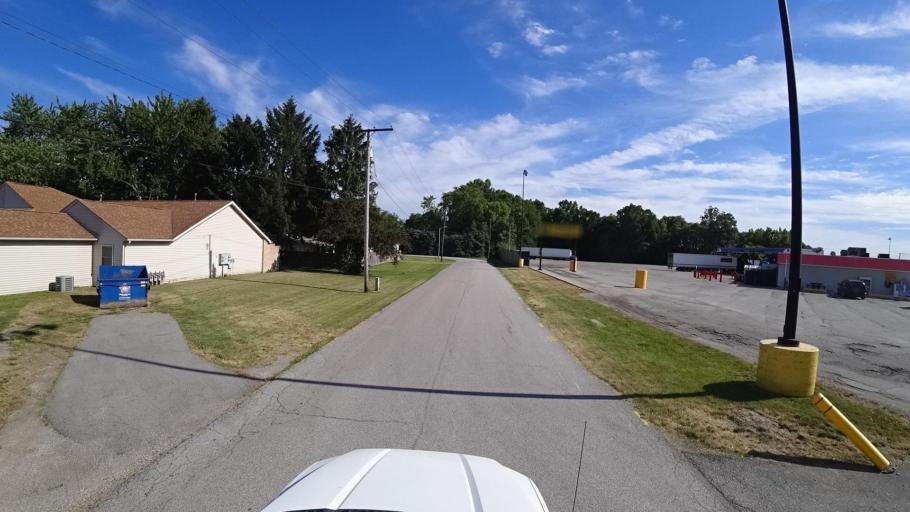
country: US
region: Indiana
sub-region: Porter County
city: Porter
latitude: 41.6133
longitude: -87.0950
